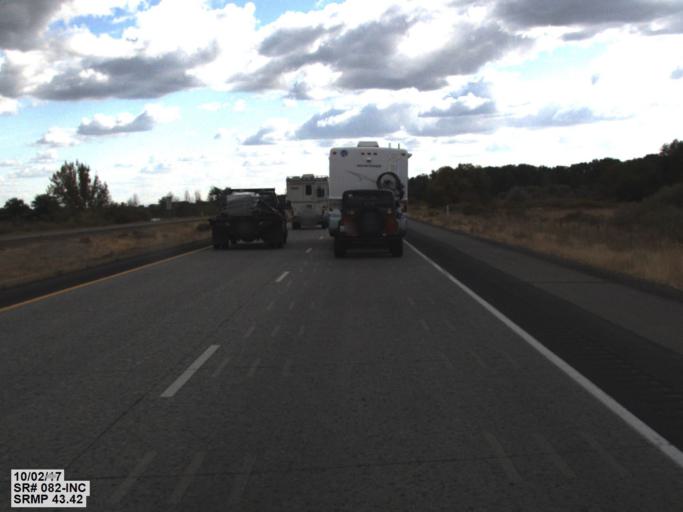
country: US
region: Washington
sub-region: Yakima County
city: Wapato
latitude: 46.4812
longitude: -120.4082
